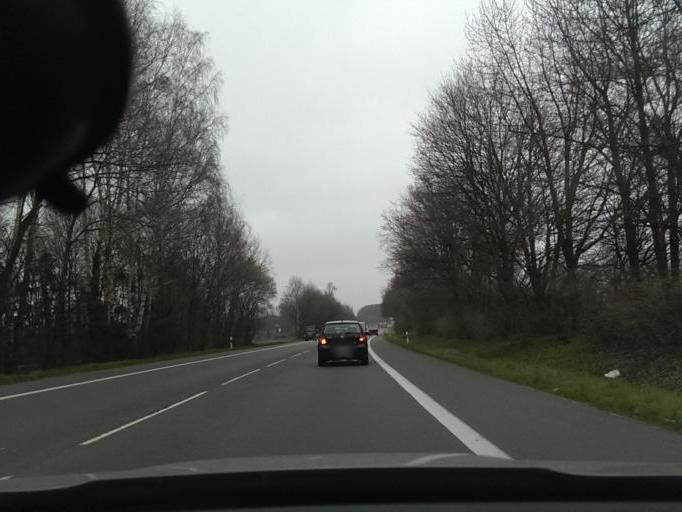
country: DE
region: North Rhine-Westphalia
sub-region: Regierungsbezirk Detmold
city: Delbruck
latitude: 51.7755
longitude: 8.5258
